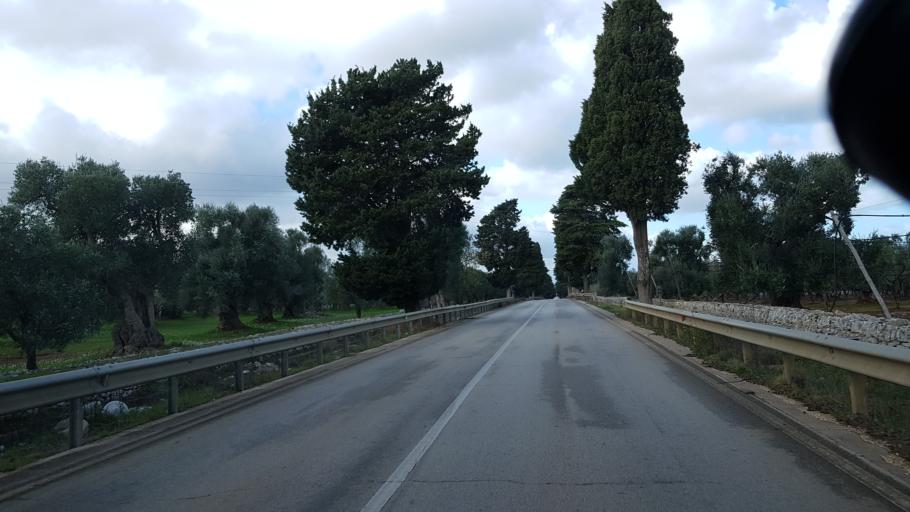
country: IT
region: Apulia
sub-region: Provincia di Brindisi
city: Montalbano
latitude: 40.7603
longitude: 17.5295
